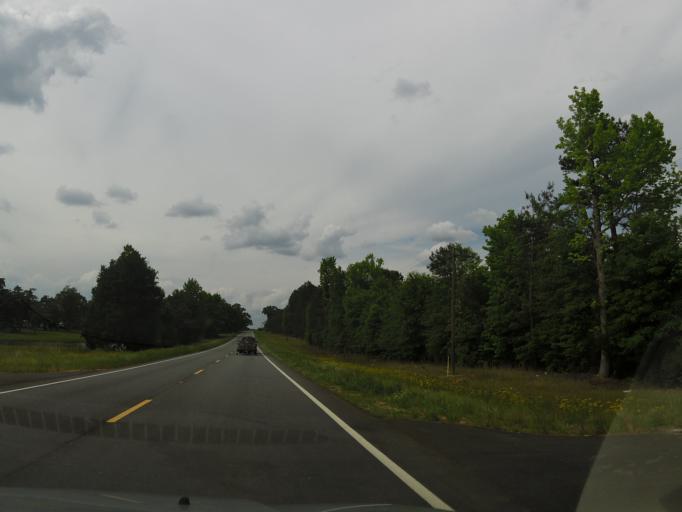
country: US
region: Georgia
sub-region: McDuffie County
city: Thomson
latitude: 33.4207
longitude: -82.4842
